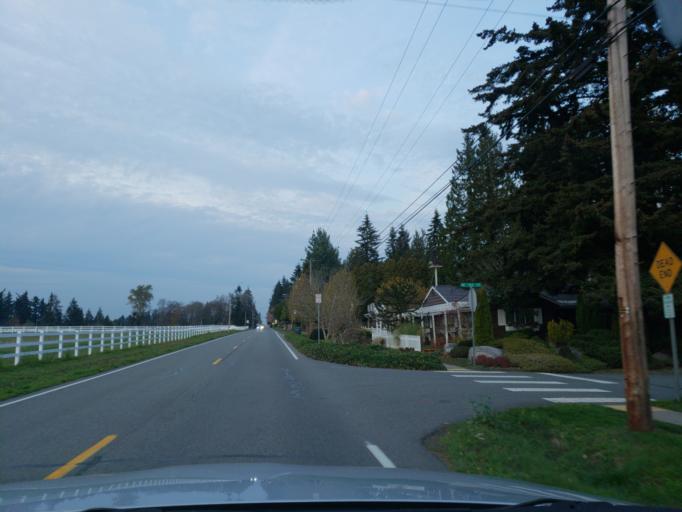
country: US
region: Washington
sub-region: King County
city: Bothell
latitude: 47.7629
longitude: -122.2232
